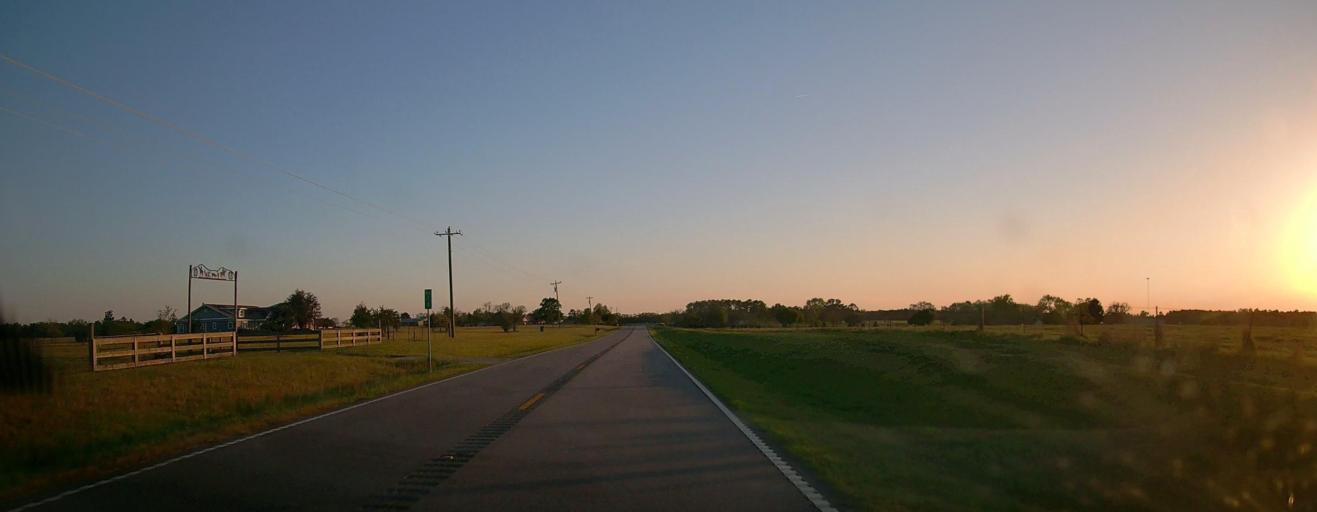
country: US
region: Georgia
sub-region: Marion County
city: Buena Vista
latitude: 32.4881
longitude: -84.6209
